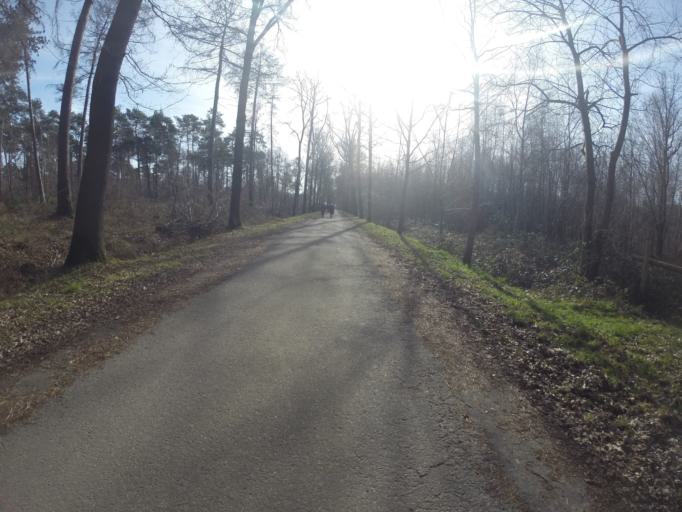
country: BE
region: Flanders
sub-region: Provincie West-Vlaanderen
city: Oostkamp
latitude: 51.1244
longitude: 3.2377
